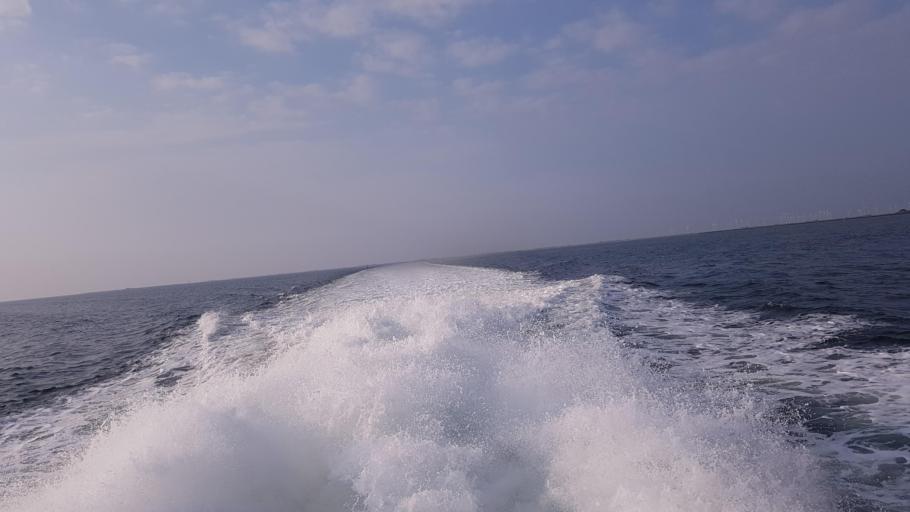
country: DE
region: Schleswig-Holstein
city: Ockholm
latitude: 54.5871
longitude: 8.7954
